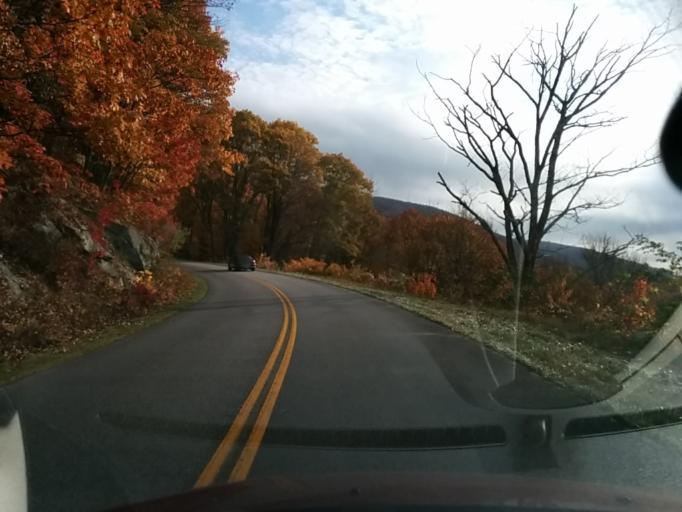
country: US
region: Virginia
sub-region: City of Buena Vista
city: Buena Vista
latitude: 37.8206
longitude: -79.1773
